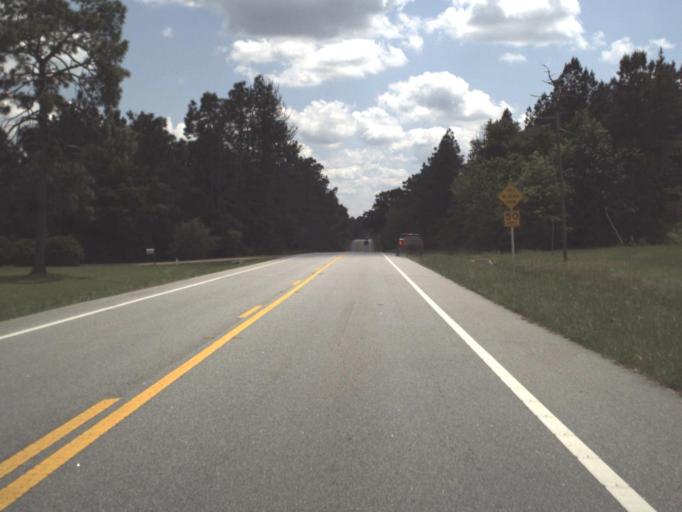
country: US
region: Florida
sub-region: Escambia County
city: Molino
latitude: 30.8289
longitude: -87.4355
